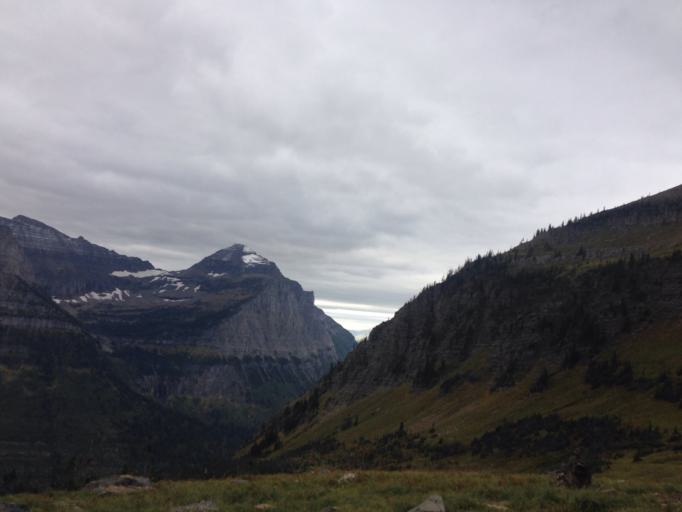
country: US
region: Montana
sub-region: Flathead County
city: Columbia Falls
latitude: 48.7337
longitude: -113.7216
